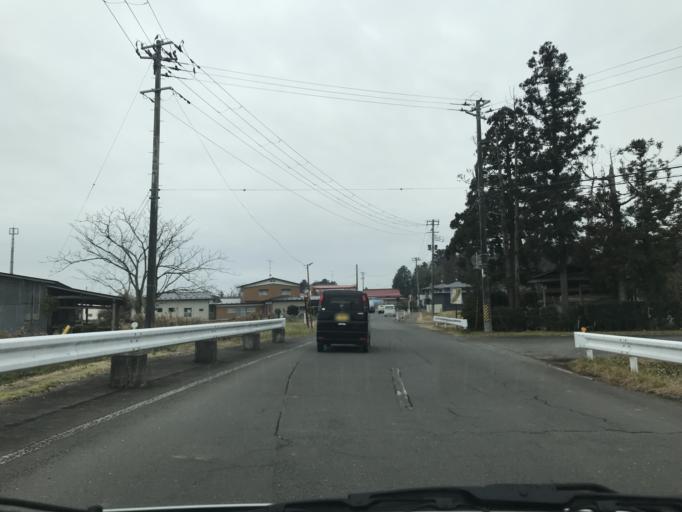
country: JP
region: Miyagi
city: Wakuya
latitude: 38.7253
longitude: 141.2163
